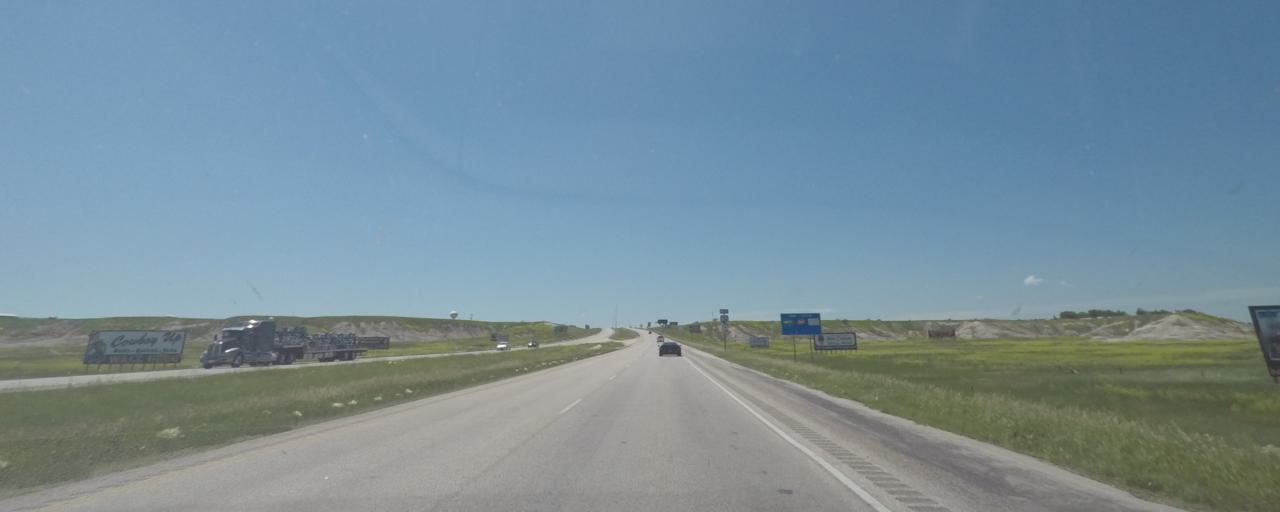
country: US
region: South Dakota
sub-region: Haakon County
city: Philip
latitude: 43.9875
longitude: -102.2220
